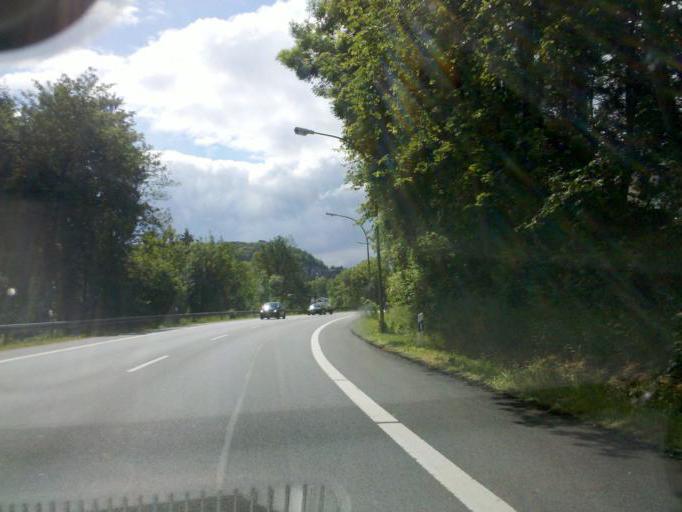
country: DE
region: North Rhine-Westphalia
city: Warstein
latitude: 51.4549
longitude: 8.3509
